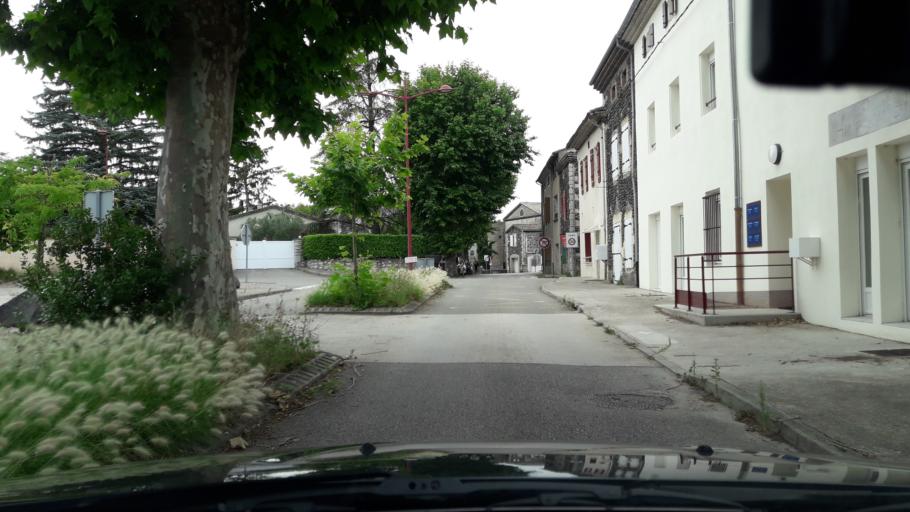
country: FR
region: Rhone-Alpes
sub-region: Departement de l'Ardeche
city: Saint-Julien-en-Saint-Alban
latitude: 44.7122
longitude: 4.7127
